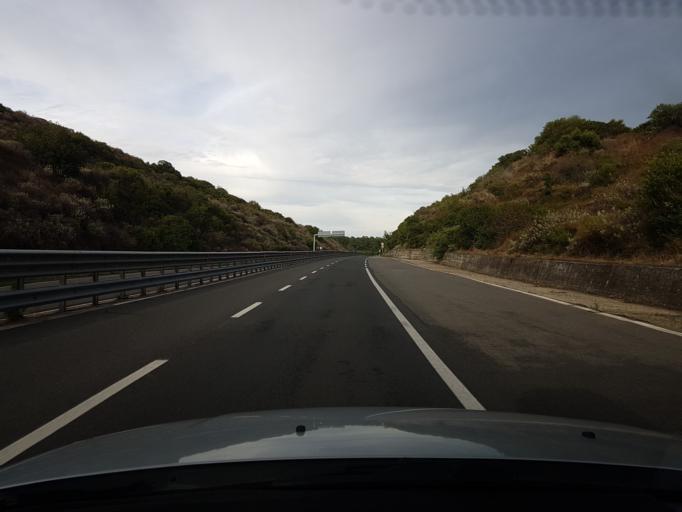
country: IT
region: Sardinia
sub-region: Provincia di Oristano
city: Soddi
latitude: 40.1478
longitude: 8.8831
